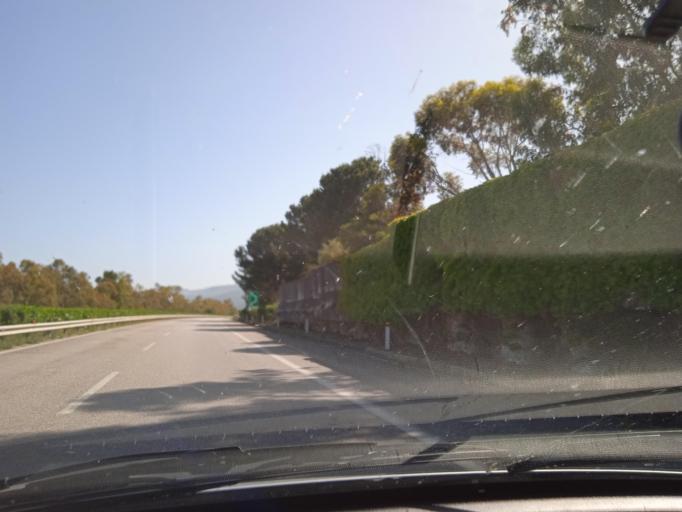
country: IT
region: Sicily
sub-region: Messina
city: Torrenova
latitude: 38.0910
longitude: 14.6959
